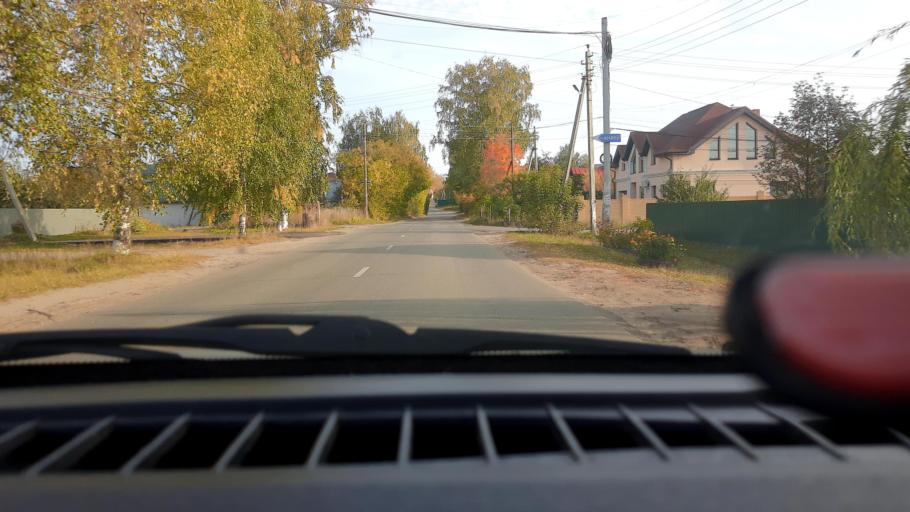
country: RU
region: Nizjnij Novgorod
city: Lukino
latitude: 56.4073
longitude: 43.7106
